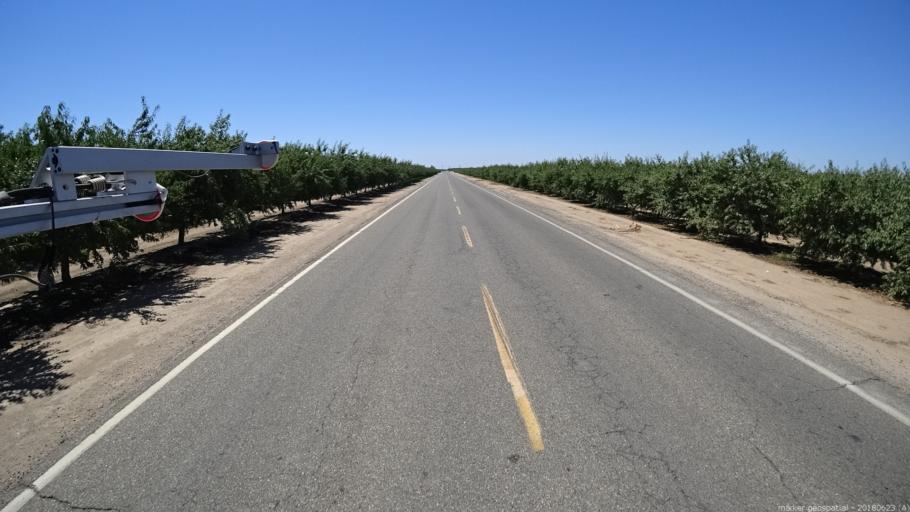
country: US
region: California
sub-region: Madera County
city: Fairmead
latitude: 37.0904
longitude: -120.2294
